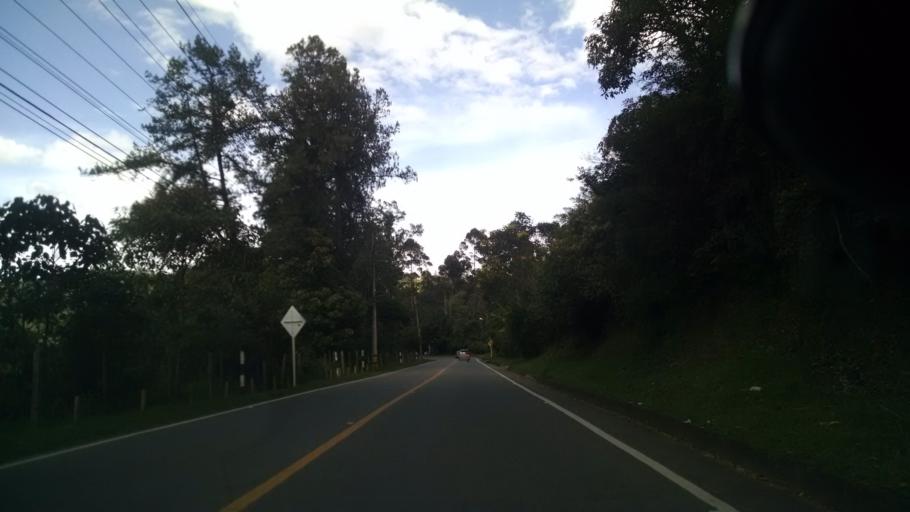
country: CO
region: Antioquia
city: El Retiro
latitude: 6.0886
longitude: -75.4910
